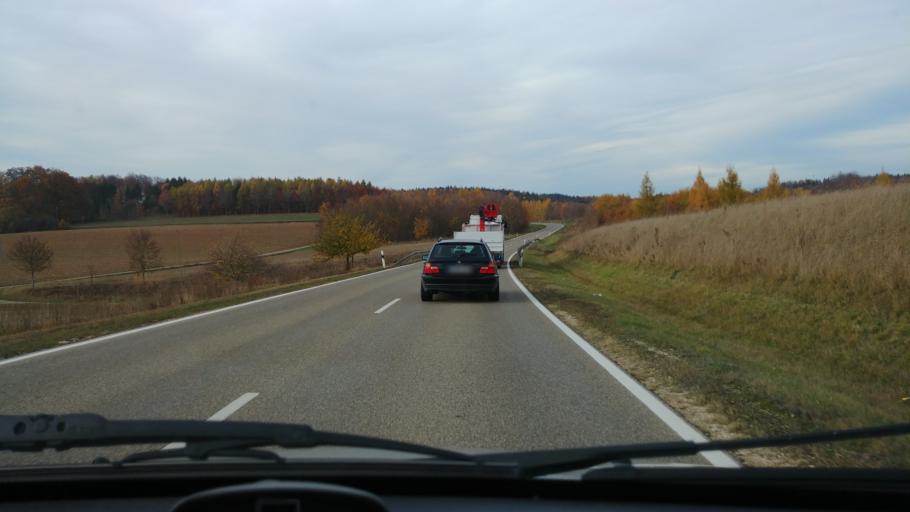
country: DE
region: Baden-Wuerttemberg
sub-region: Regierungsbezirk Stuttgart
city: Giengen an der Brenz
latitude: 48.6558
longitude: 10.2719
